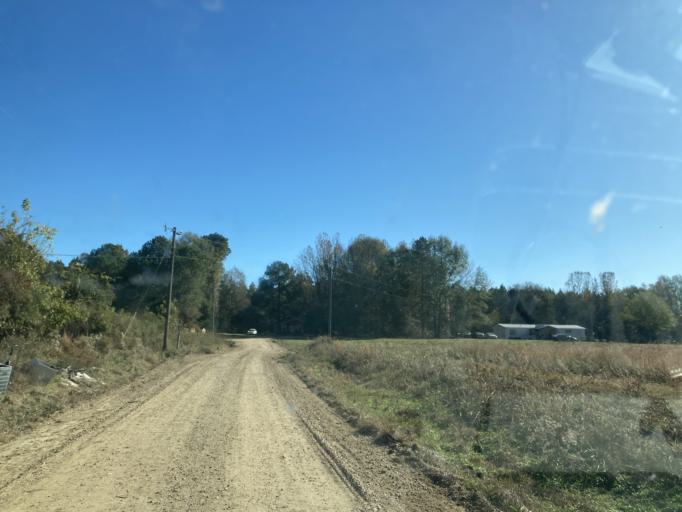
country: US
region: Mississippi
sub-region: Madison County
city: Kearney Park
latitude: 32.6709
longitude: -90.3402
